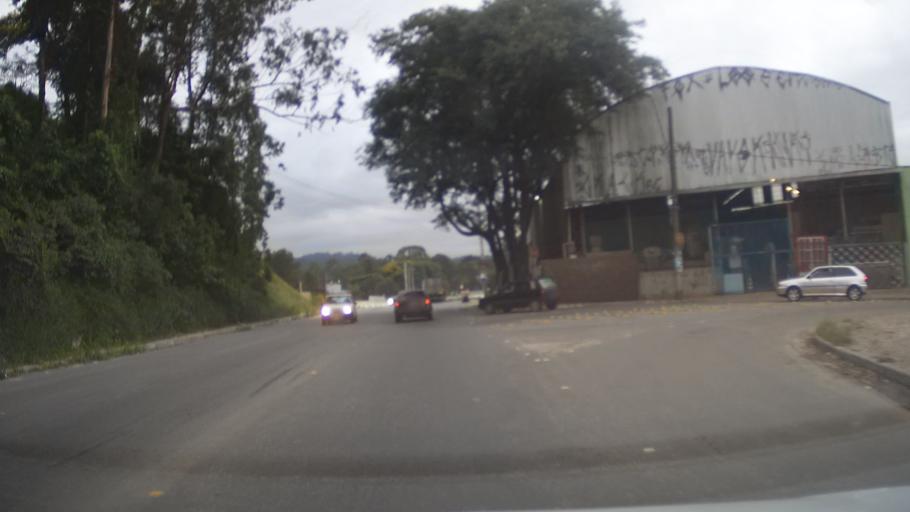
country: BR
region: Sao Paulo
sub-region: Guarulhos
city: Guarulhos
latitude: -23.3905
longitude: -46.4430
